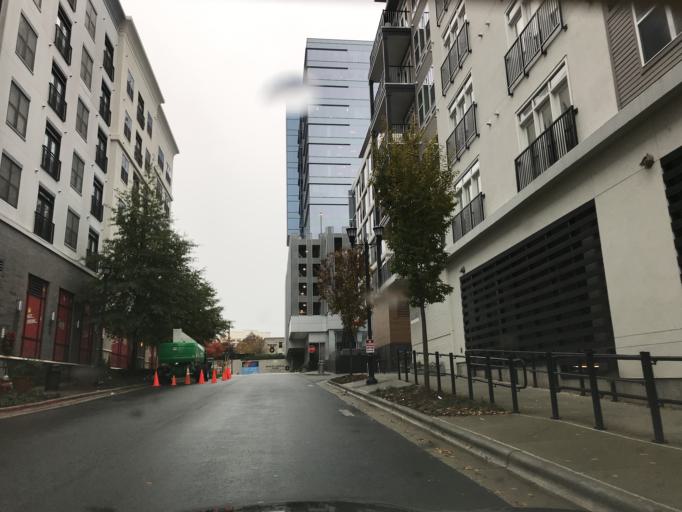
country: US
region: North Carolina
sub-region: Wake County
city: West Raleigh
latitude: 35.8381
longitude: -78.6394
